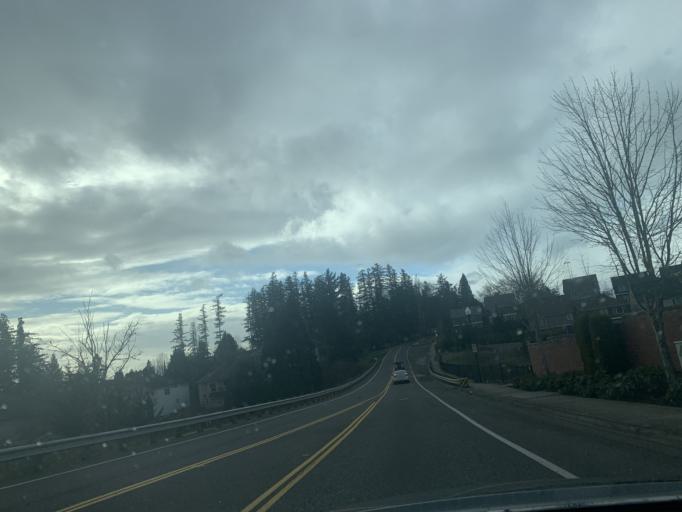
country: US
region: Oregon
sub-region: Washington County
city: Bethany
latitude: 45.5638
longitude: -122.8494
